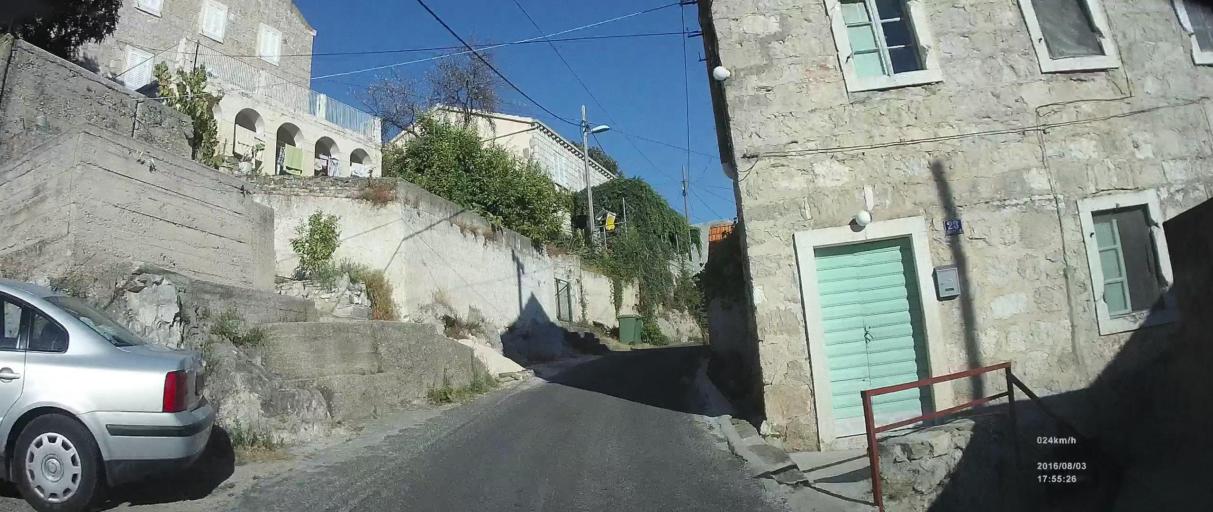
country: HR
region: Dubrovacko-Neretvanska
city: Blato
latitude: 42.7367
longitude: 17.5462
